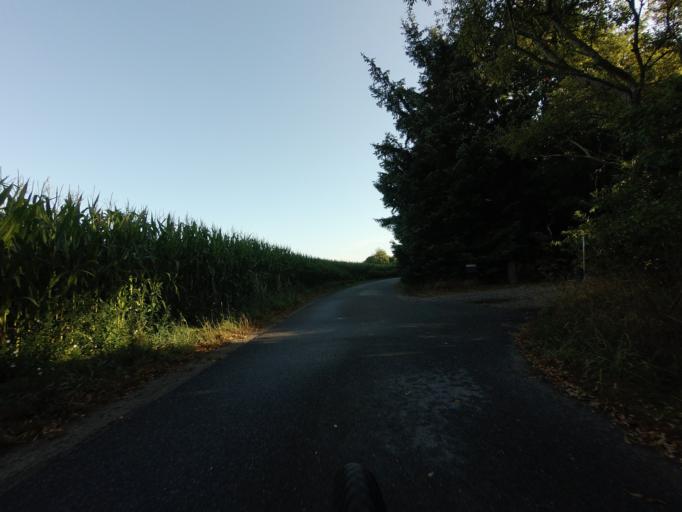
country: DK
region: North Denmark
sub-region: Hjorring Kommune
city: Vra
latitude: 57.3664
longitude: 9.8648
